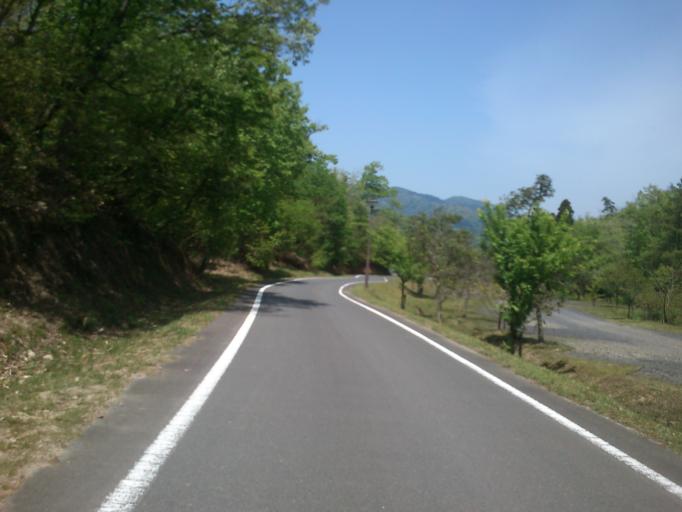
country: JP
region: Kyoto
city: Miyazu
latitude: 35.6216
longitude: 135.2389
